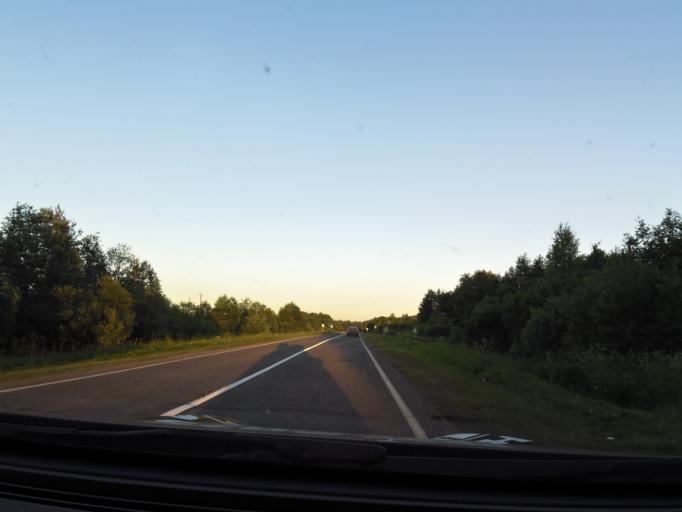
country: RU
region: Jaroslavl
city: Prechistoye
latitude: 58.3797
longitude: 40.4761
